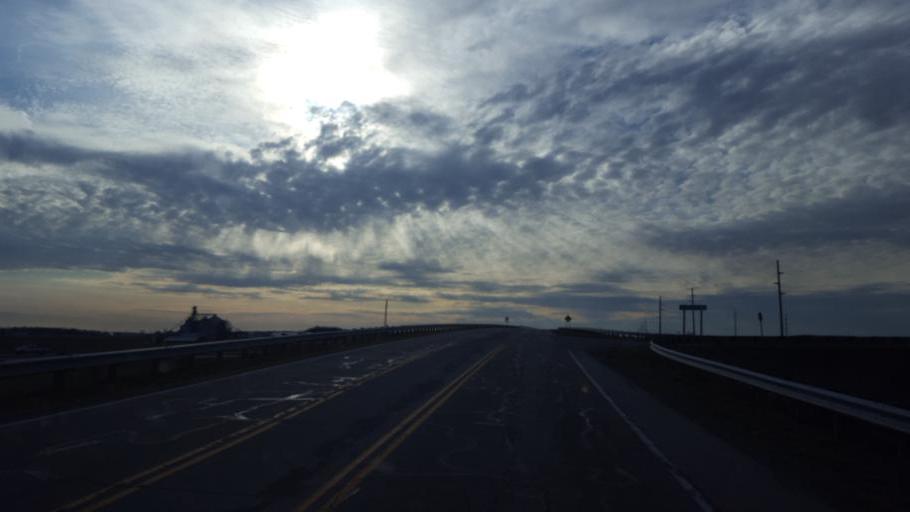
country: US
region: Ohio
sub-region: Crawford County
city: Bucyrus
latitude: 40.7839
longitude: -82.8983
